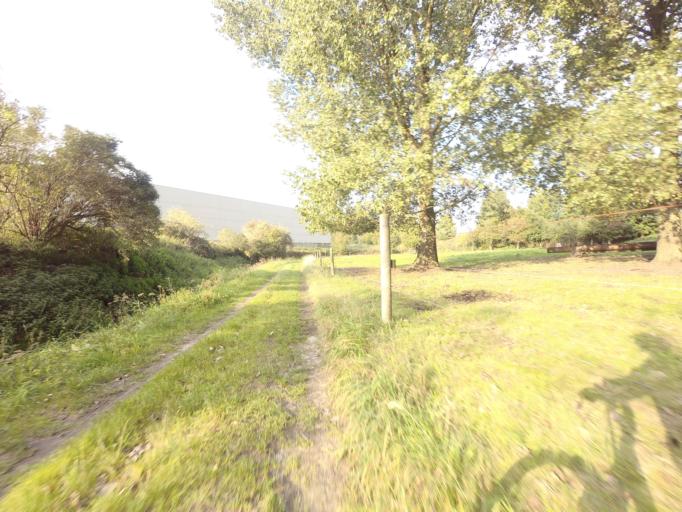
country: BE
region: Flanders
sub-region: Provincie Antwerpen
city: Willebroek
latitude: 51.0613
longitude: 4.3725
